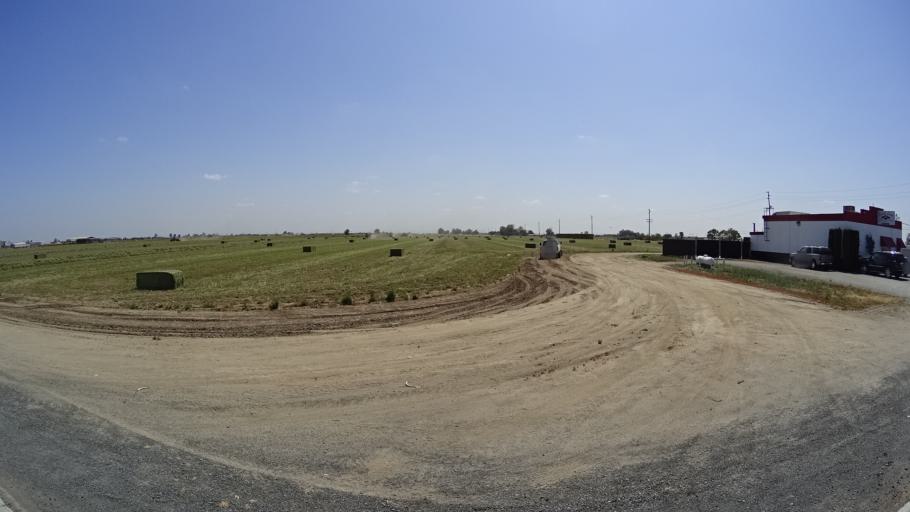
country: US
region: California
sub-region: Kings County
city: Home Garden
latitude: 36.3143
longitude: -119.6190
